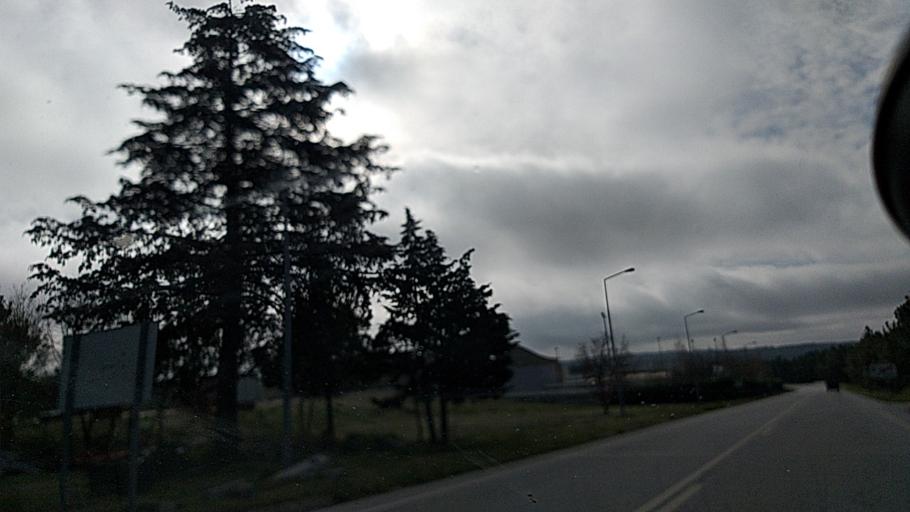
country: PT
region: Guarda
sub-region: Aguiar da Beira
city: Aguiar da Beira
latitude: 40.8156
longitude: -7.5371
